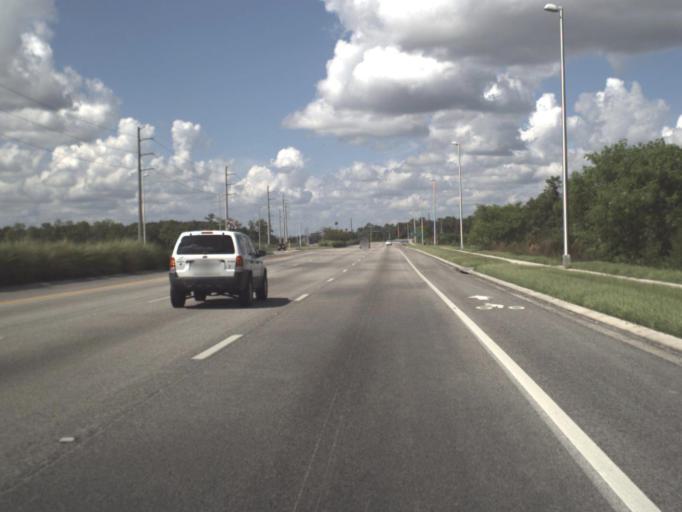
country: US
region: Florida
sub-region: Lee County
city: Gateway
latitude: 26.6226
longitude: -81.7722
